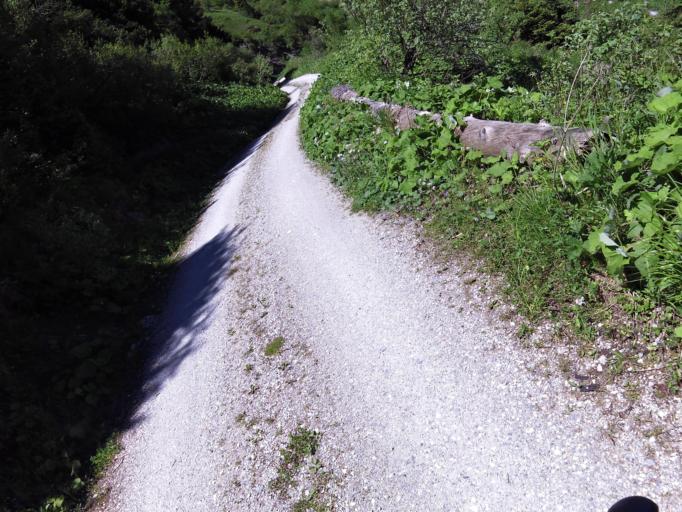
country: AT
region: Tyrol
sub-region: Politischer Bezirk Innsbruck Land
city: Neustift im Stubaital
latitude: 47.1212
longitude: 11.2872
